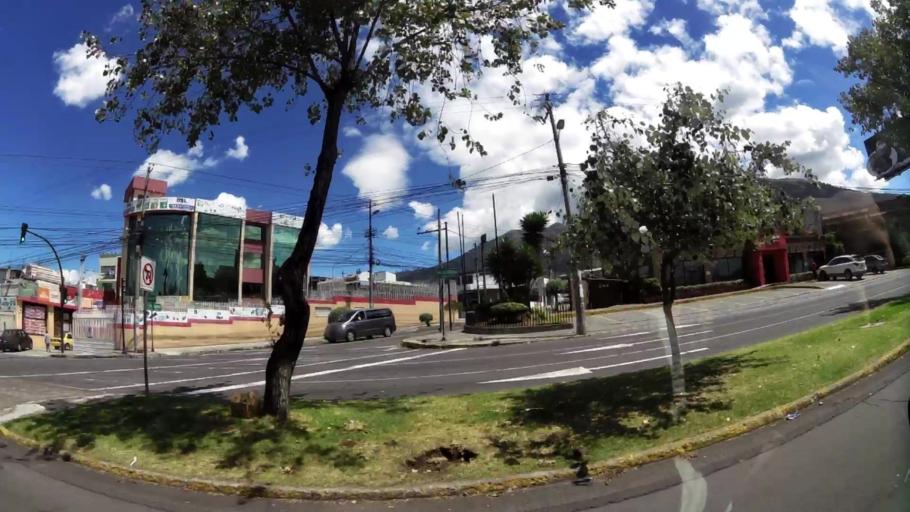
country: EC
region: Pichincha
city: Quito
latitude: -0.1769
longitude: -78.4923
